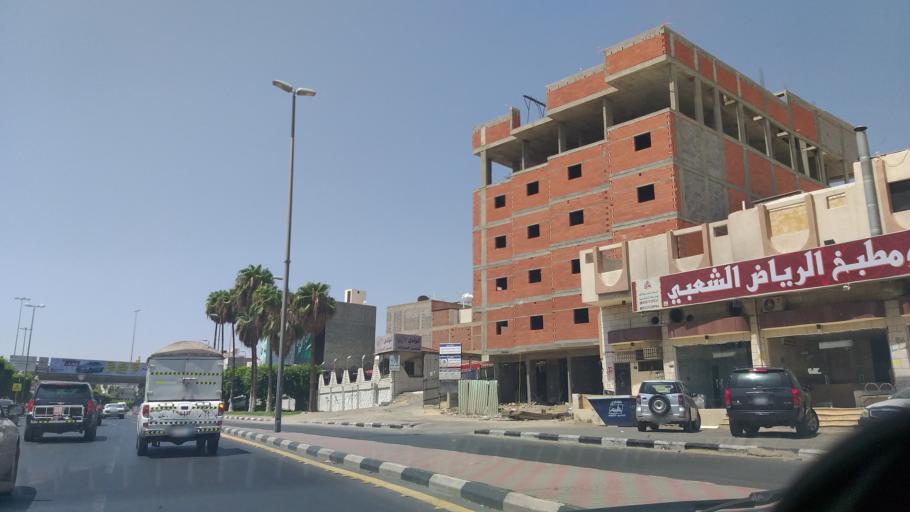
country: SA
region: Makkah
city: Ta'if
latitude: 21.2763
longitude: 40.4223
